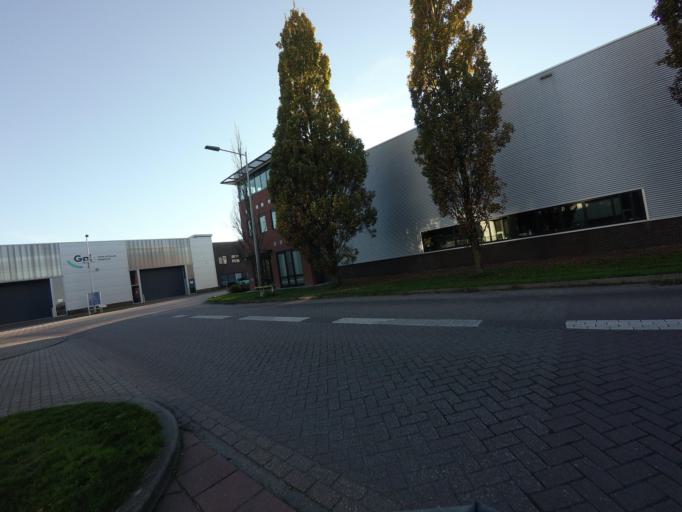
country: NL
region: Utrecht
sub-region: Gemeente Lopik
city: Lopik
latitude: 51.9876
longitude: 4.9678
